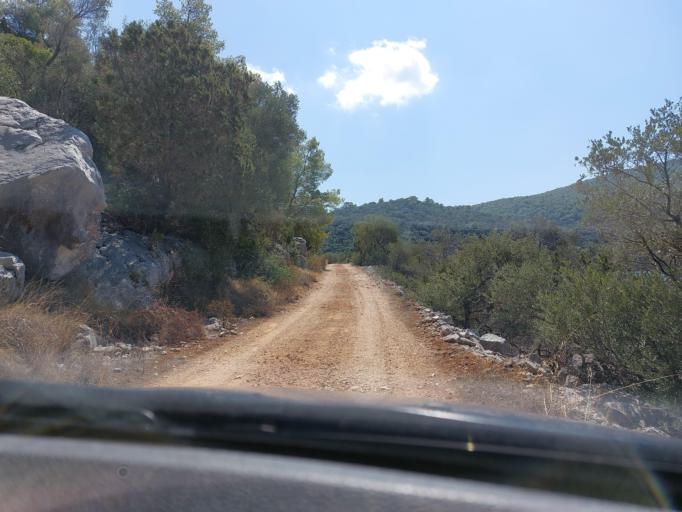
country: HR
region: Dubrovacko-Neretvanska
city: Smokvica
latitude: 42.7743
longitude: 16.8372
